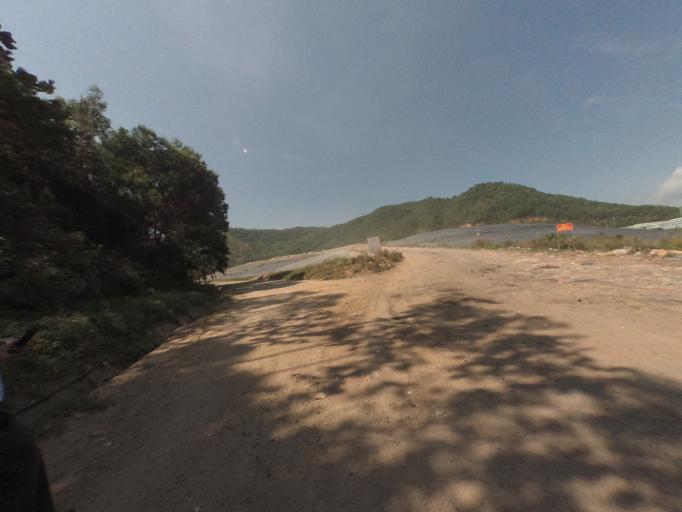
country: VN
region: Da Nang
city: Lien Chieu
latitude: 16.0445
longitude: 108.1422
